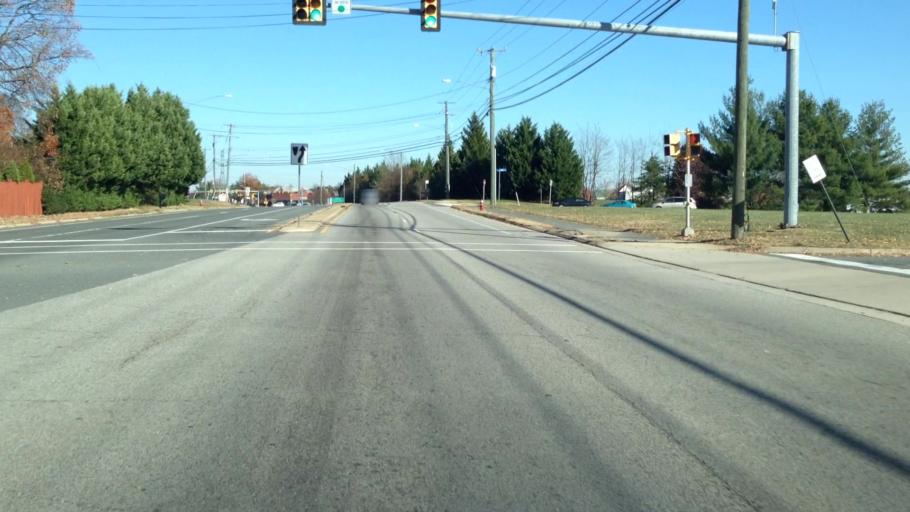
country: US
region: Virginia
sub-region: Fairfax County
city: Franconia
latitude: 38.7624
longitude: -77.1575
